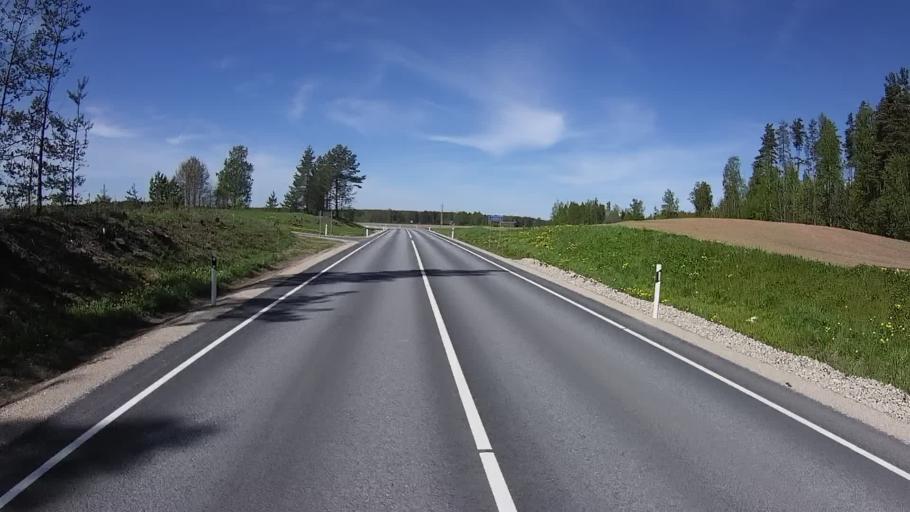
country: EE
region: Polvamaa
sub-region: Polva linn
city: Polva
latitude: 58.0950
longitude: 27.1564
